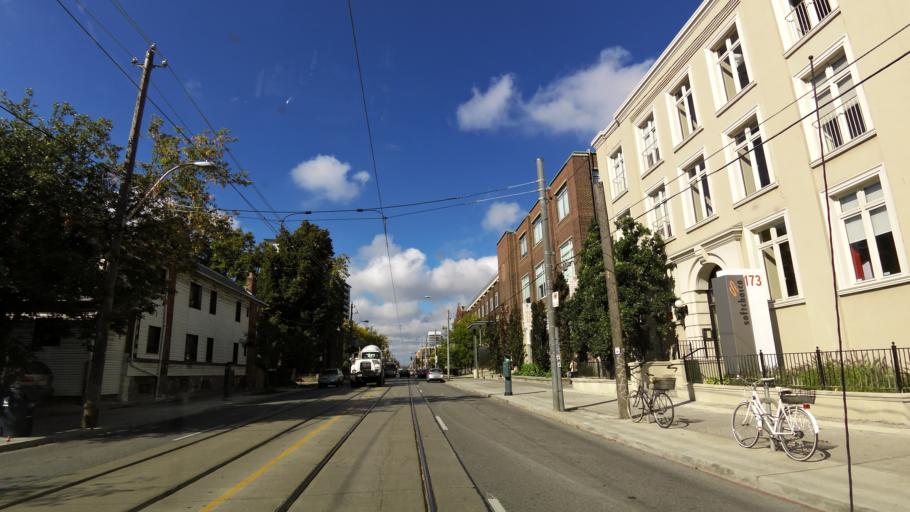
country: CA
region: Ontario
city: Toronto
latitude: 43.6358
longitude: -79.4262
